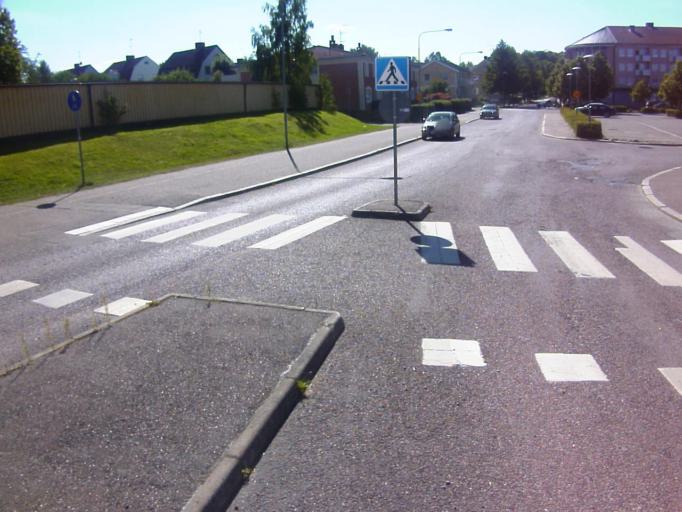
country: SE
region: Soedermanland
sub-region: Eskilstuna Kommun
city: Eskilstuna
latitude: 59.3747
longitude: 16.5313
